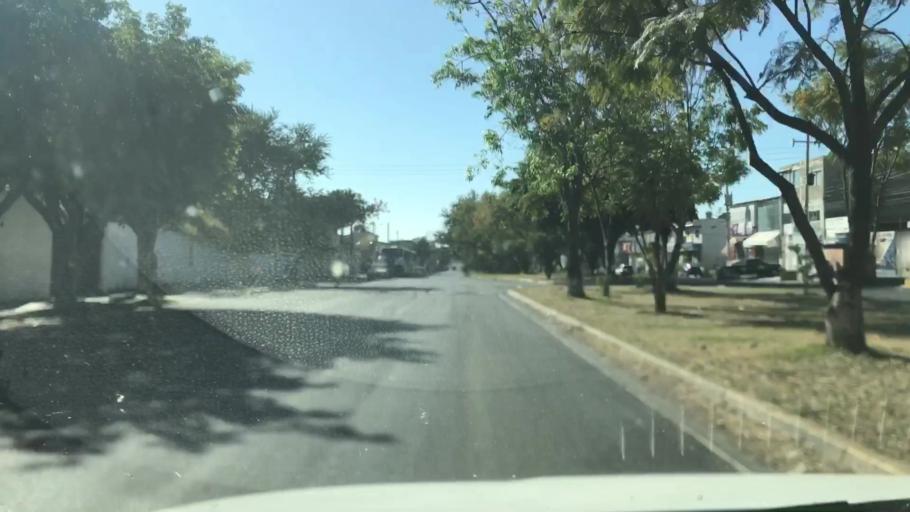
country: MX
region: Jalisco
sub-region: Tlajomulco de Zuniga
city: Palomar
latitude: 20.6334
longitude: -103.4448
